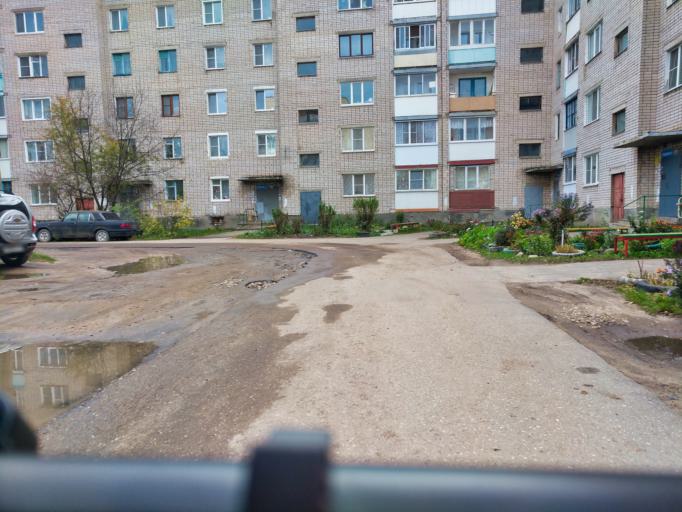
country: RU
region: Tverskaya
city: Rzhev
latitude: 56.2476
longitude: 34.3308
